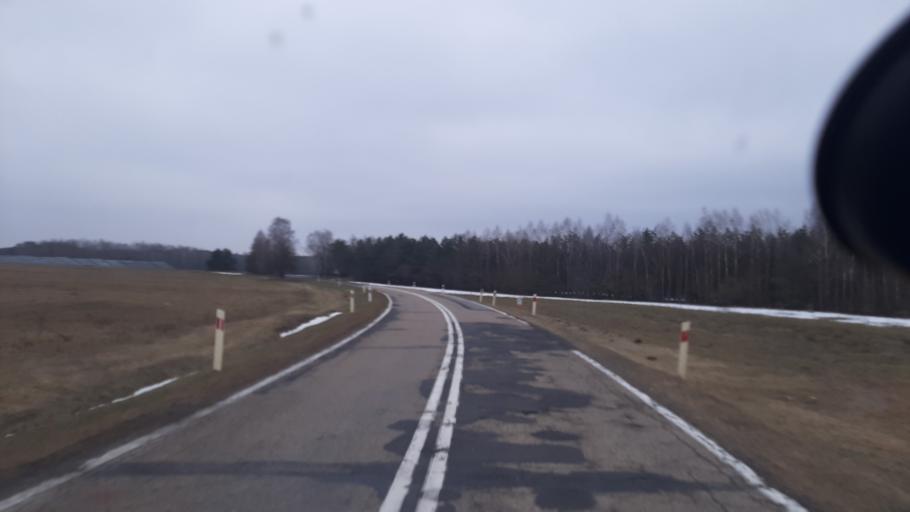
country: PL
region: Lublin Voivodeship
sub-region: Powiat wlodawski
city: Wlodawa
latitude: 51.5139
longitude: 23.5699
